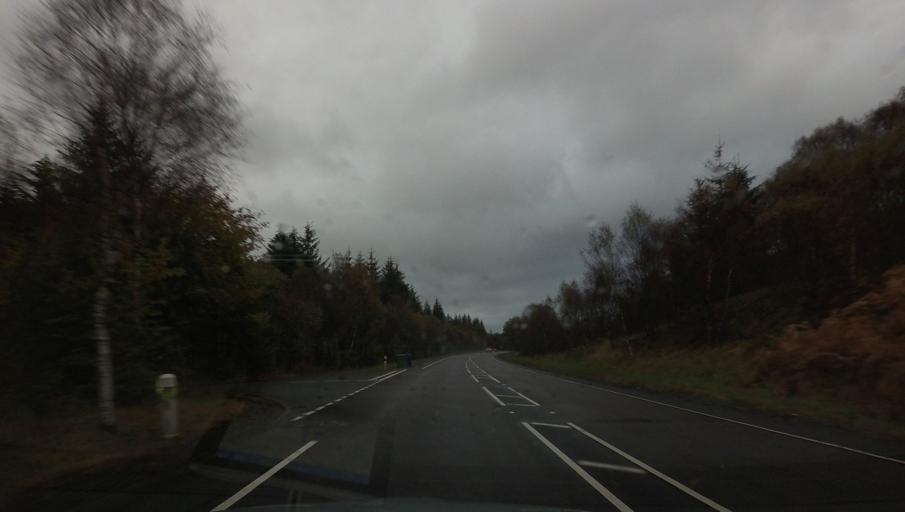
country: GB
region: Scotland
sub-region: Stirling
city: Callander
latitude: 56.4147
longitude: -4.5175
